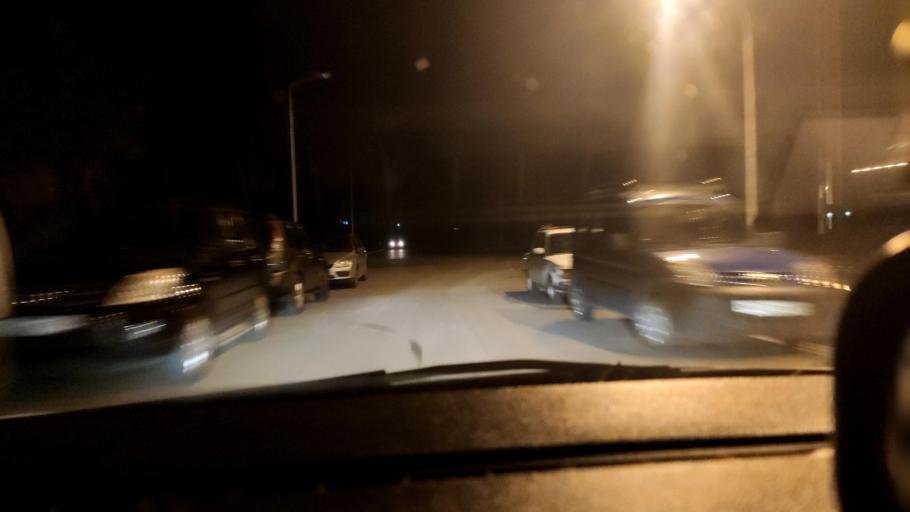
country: RU
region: Voronezj
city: Shilovo
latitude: 51.5736
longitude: 39.1299
